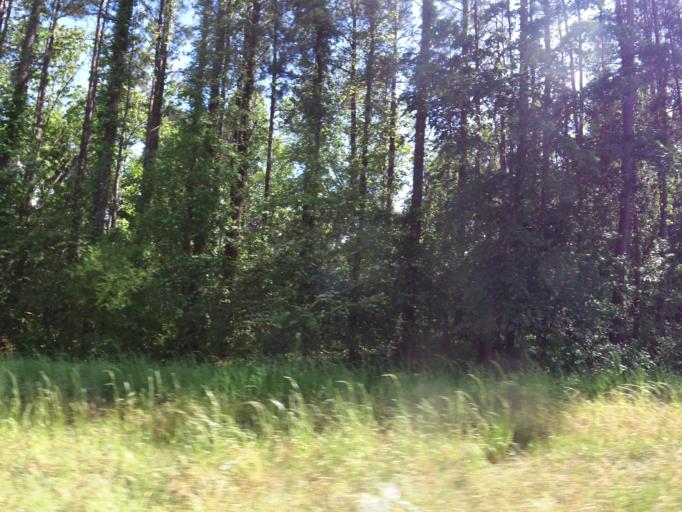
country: US
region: South Carolina
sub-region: Bamberg County
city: Denmark
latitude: 33.3433
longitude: -81.1899
